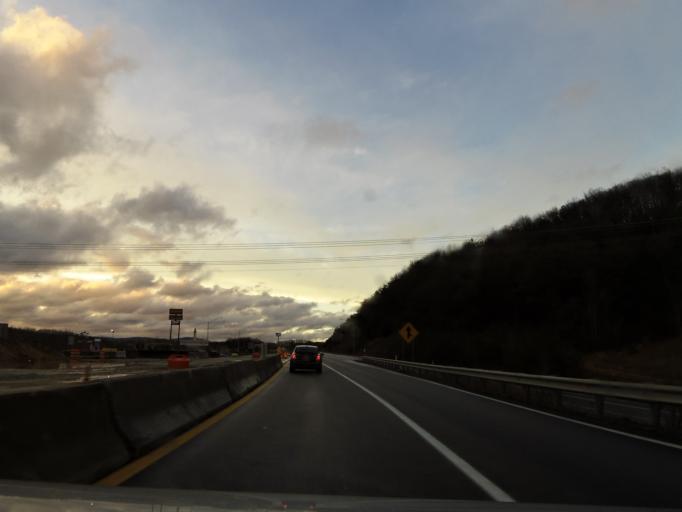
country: US
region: Tennessee
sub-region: Campbell County
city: Jacksboro
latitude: 36.3786
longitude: -84.2458
